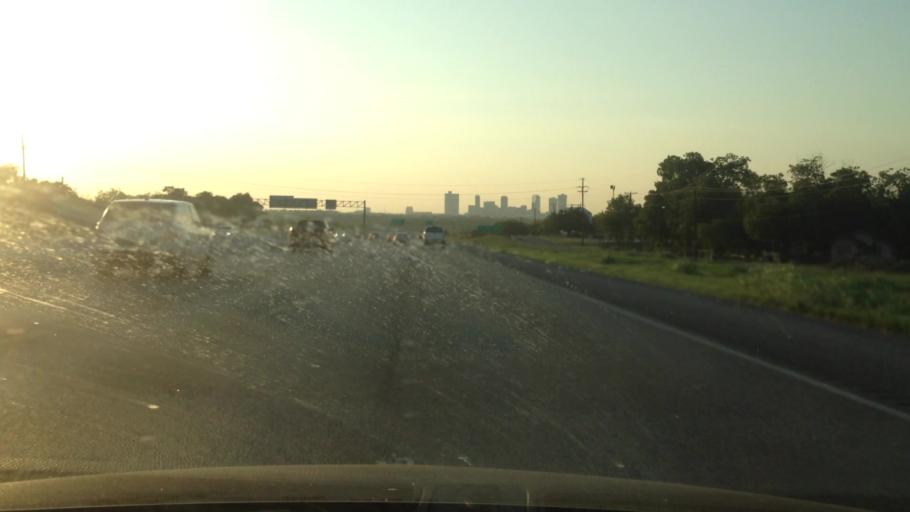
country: US
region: Texas
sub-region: Tarrant County
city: Fort Worth
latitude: 32.7153
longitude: -97.2818
